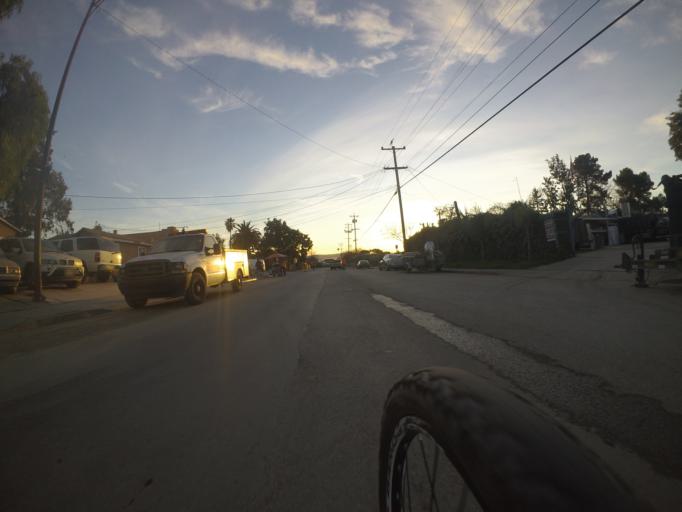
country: US
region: California
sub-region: Santa Clara County
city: Milpitas
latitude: 37.4282
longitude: -121.9733
